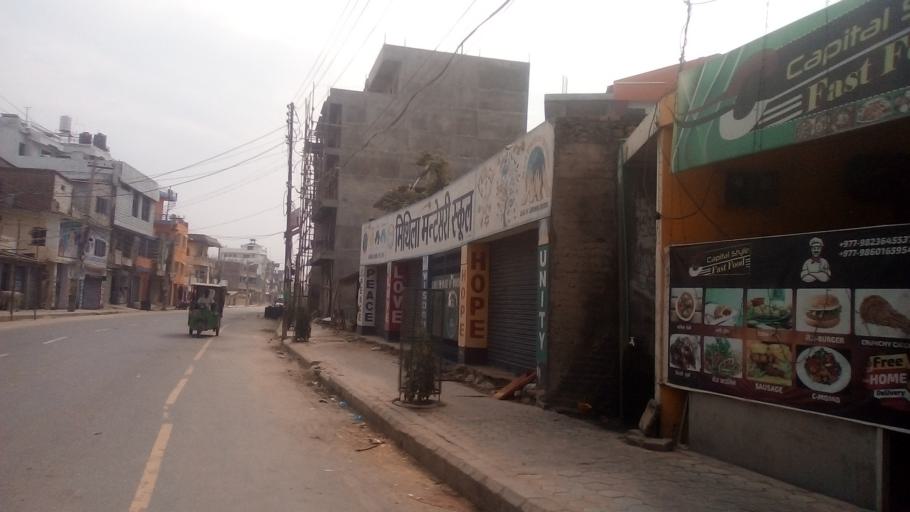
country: NP
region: Central Region
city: Janakpur
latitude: 26.7308
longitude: 85.9335
